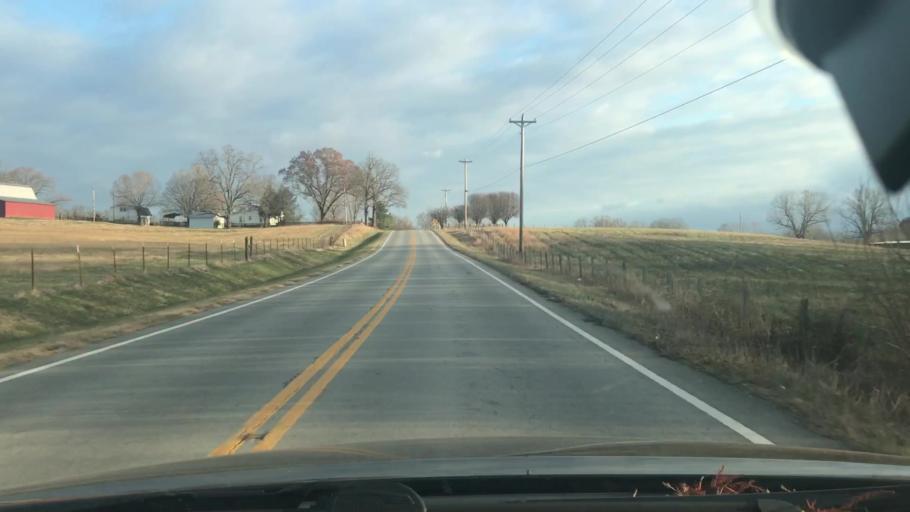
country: US
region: Tennessee
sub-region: Dickson County
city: Charlotte
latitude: 36.2079
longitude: -87.2828
